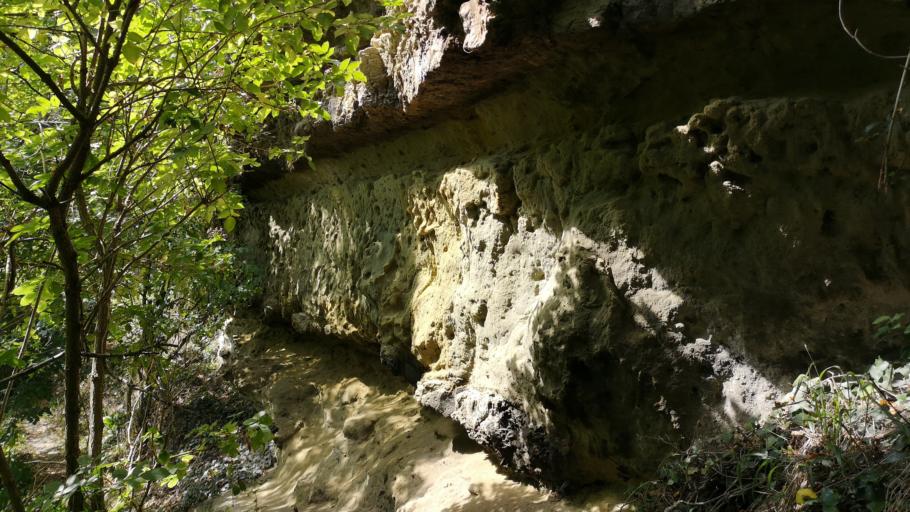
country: GB
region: England
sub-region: Isle of Wight
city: Ventnor
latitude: 50.5897
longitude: -1.2406
